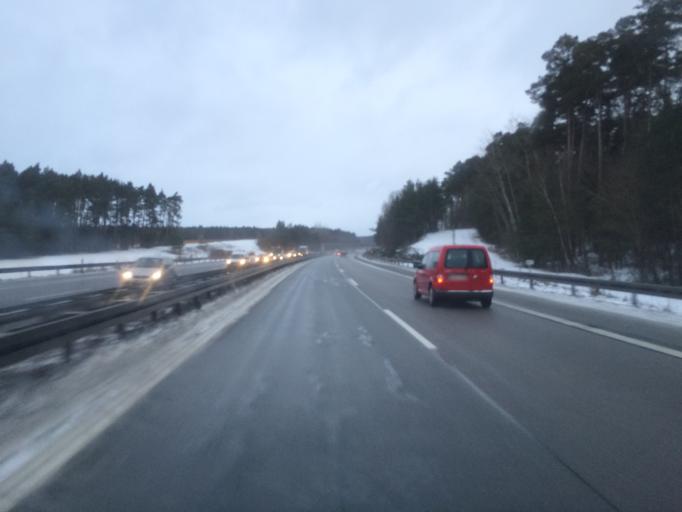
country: DE
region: Bavaria
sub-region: Upper Palatinate
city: Regenstauf
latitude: 49.1436
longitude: 12.1051
